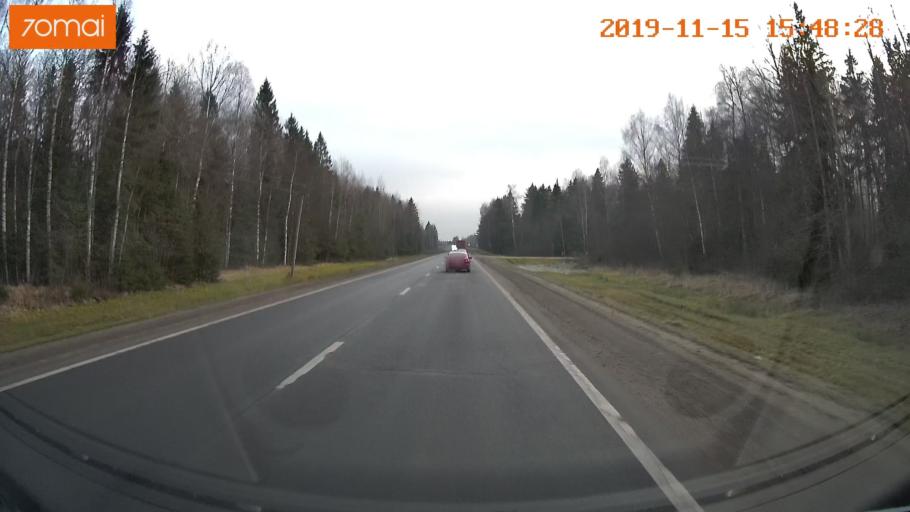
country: RU
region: Jaroslavl
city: Danilov
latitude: 57.9268
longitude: 40.0065
